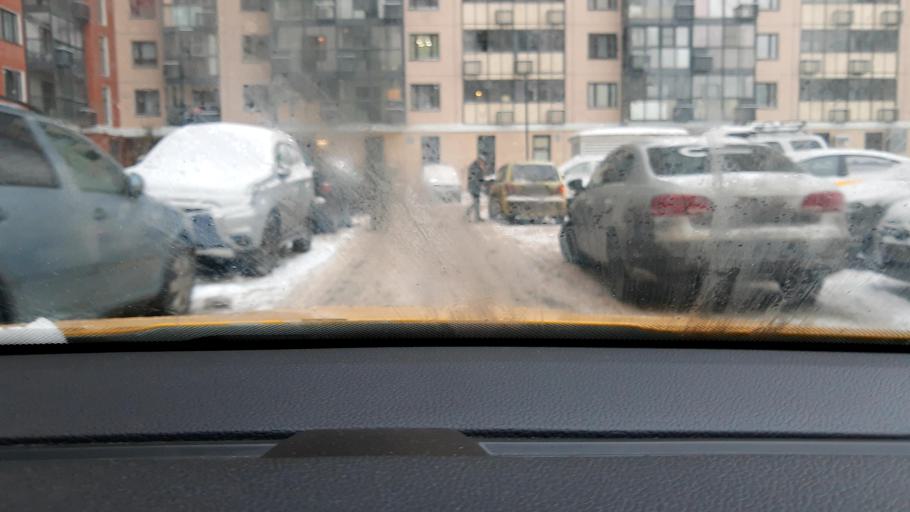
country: RU
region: Moskovskaya
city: Pavshino
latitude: 55.8606
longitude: 37.3729
